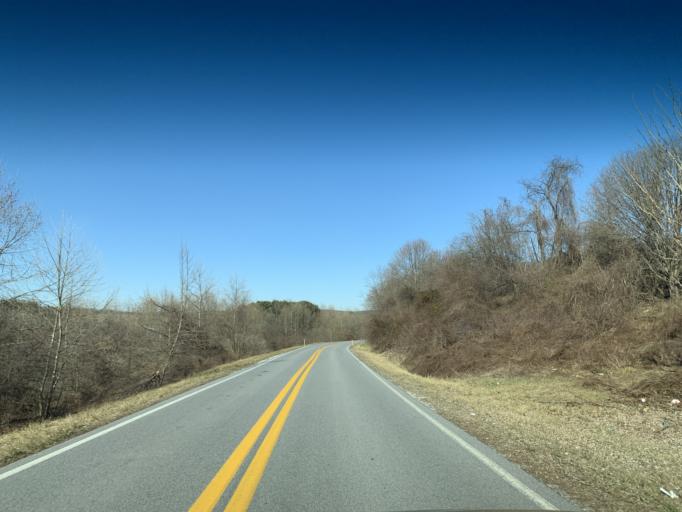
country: US
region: Maryland
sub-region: Carroll County
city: Westminster
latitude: 39.6428
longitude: -76.9644
